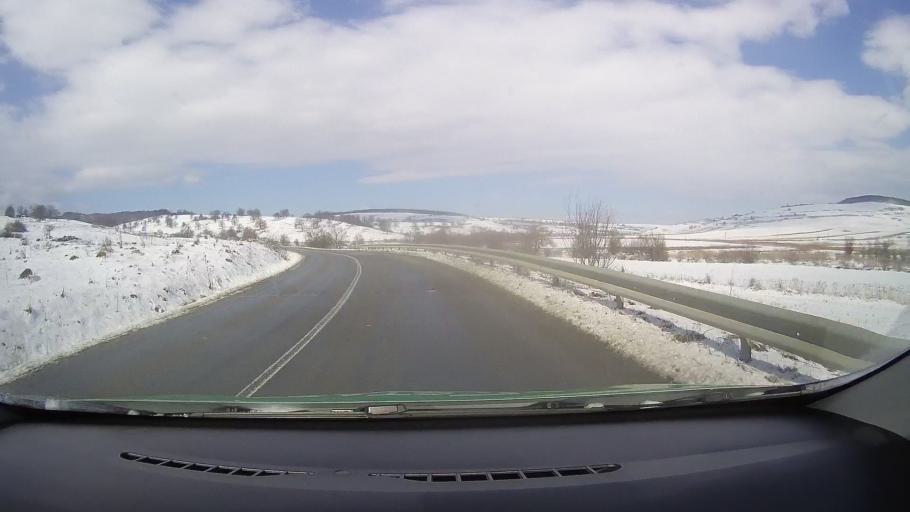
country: RO
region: Sibiu
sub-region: Comuna Altina
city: Altina
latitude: 45.9419
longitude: 24.4540
